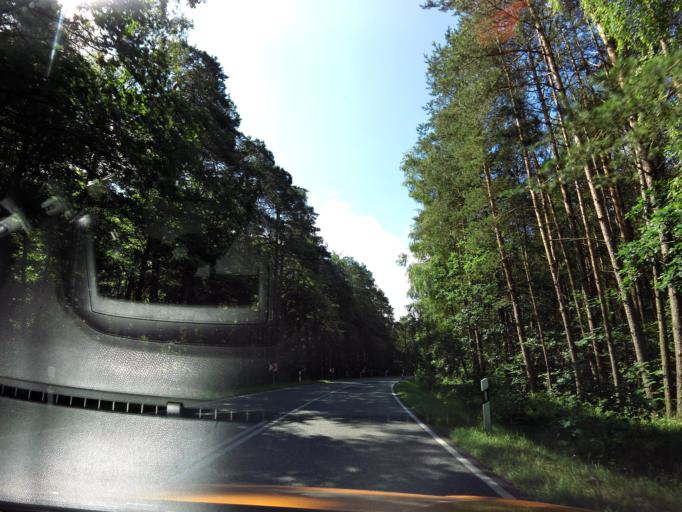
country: DE
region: Mecklenburg-Vorpommern
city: Krakow am See
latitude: 53.5611
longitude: 12.2739
